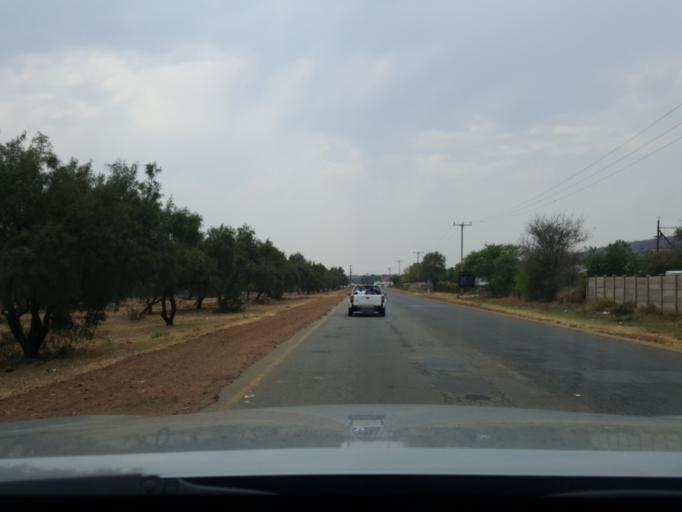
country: ZA
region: North-West
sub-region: Ngaka Modiri Molema District Municipality
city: Zeerust
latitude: -25.4982
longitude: 25.9841
